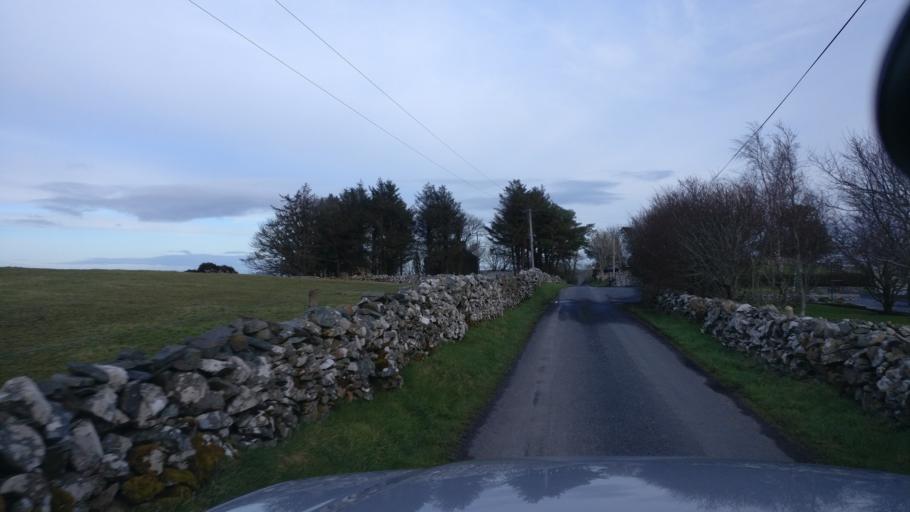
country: IE
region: Connaught
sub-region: County Galway
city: Oughterard
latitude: 53.5293
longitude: -9.3649
